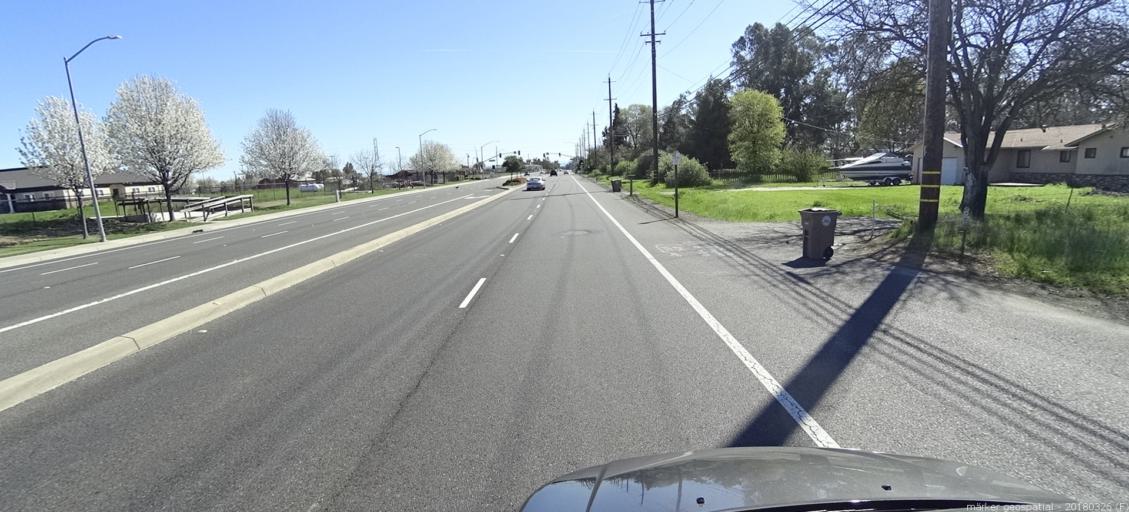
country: US
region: California
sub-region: Sacramento County
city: Vineyard
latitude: 38.4526
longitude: -121.3419
